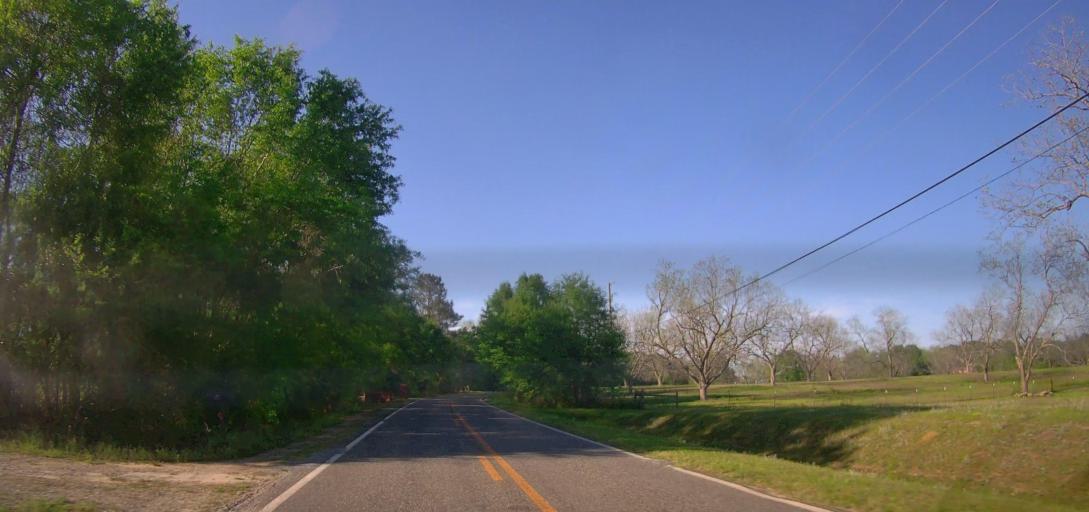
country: US
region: Georgia
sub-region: Houston County
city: Perry
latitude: 32.4790
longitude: -83.8054
